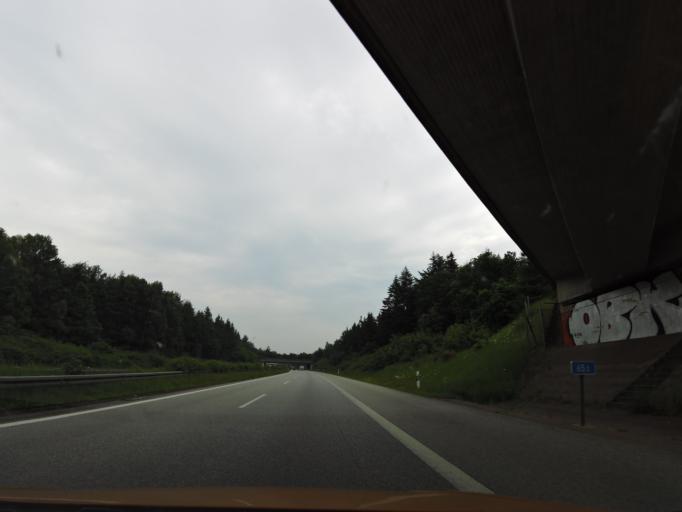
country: DE
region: Mecklenburg-Vorpommern
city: Bobitz
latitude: 53.8307
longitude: 11.3643
